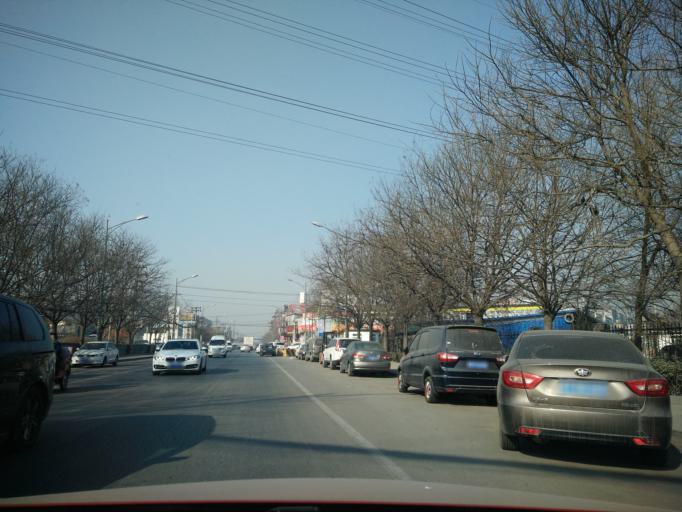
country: CN
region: Beijing
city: Jiugong
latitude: 39.8305
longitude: 116.4960
